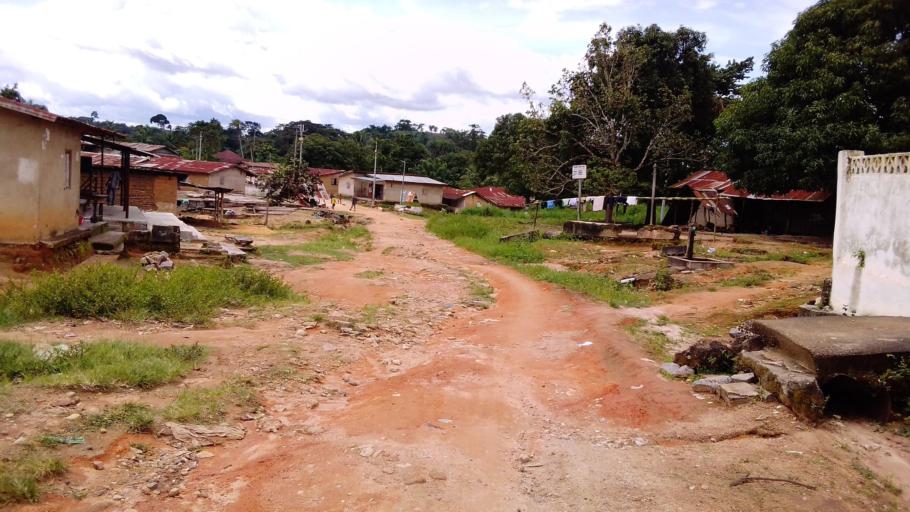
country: SL
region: Eastern Province
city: Koyima
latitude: 8.7006
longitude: -11.0089
